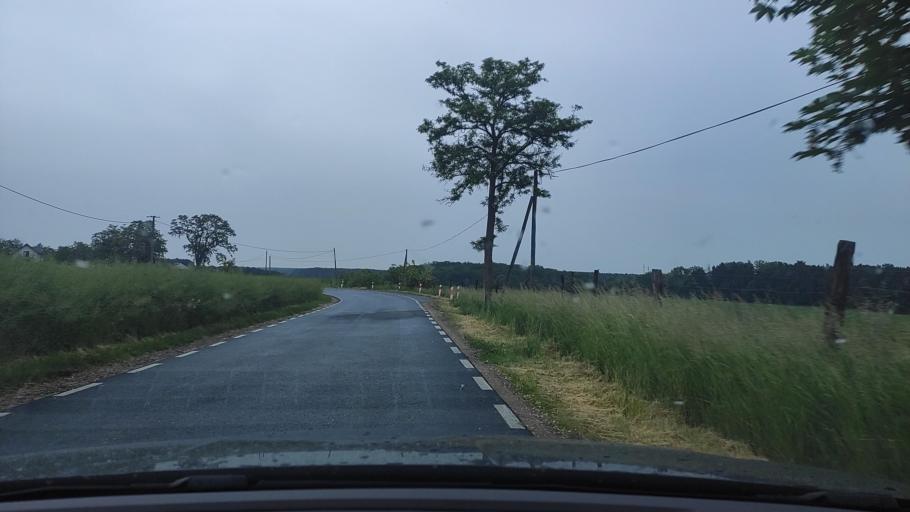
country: PL
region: Greater Poland Voivodeship
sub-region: Powiat poznanski
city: Kobylnica
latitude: 52.4834
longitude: 17.1575
